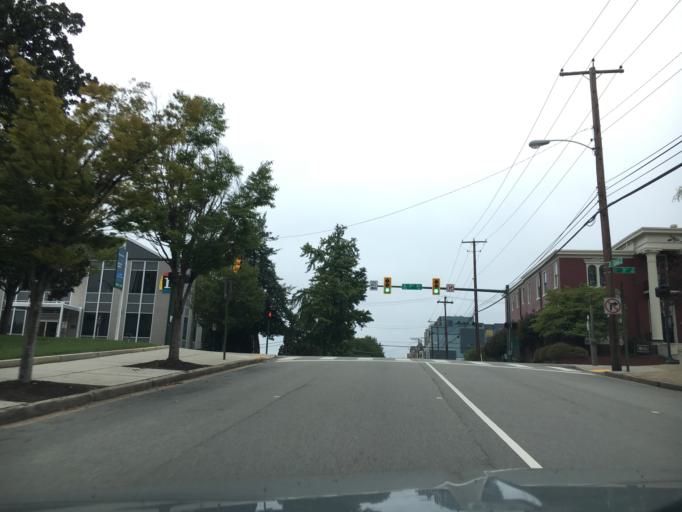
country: US
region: Virginia
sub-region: City of Richmond
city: Richmond
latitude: 37.5395
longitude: -77.4429
